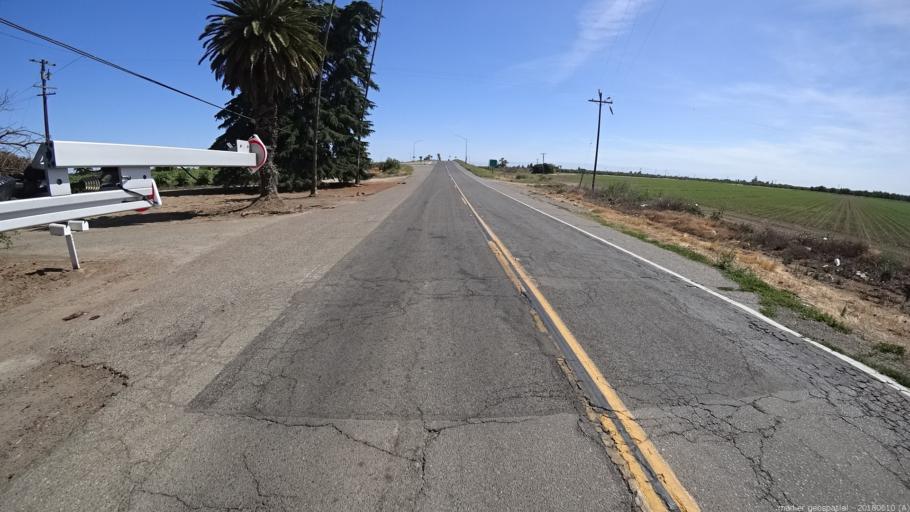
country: US
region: California
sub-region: Madera County
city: Chowchilla
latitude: 37.0814
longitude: -120.2993
